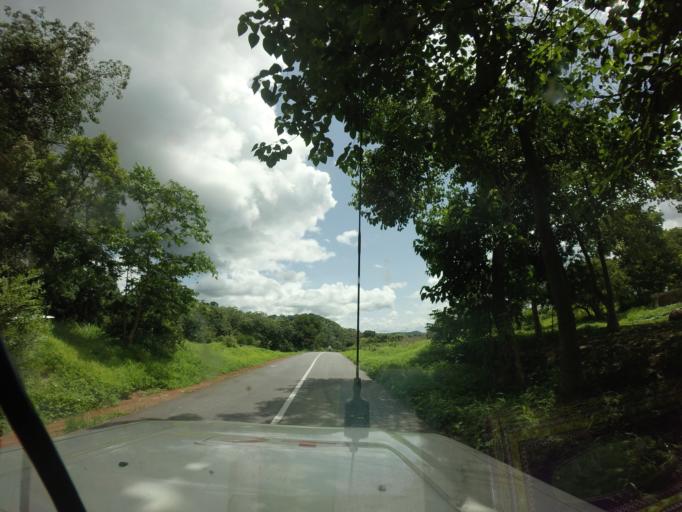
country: SL
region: Northern Province
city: Bindi
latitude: 10.1455
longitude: -11.5807
